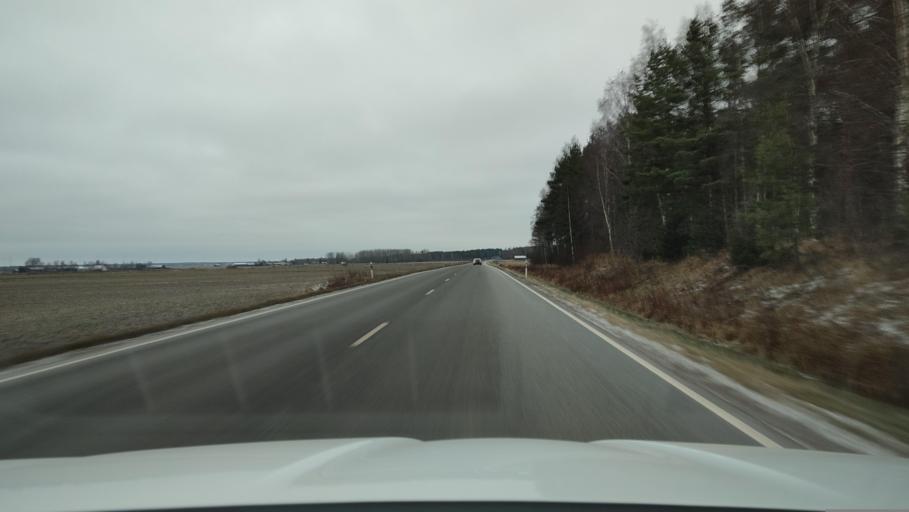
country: FI
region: Ostrobothnia
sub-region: Sydosterbotten
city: Naerpes
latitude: 62.5372
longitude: 21.4653
